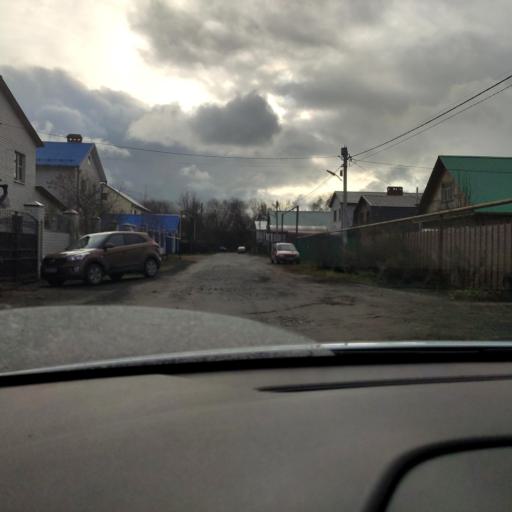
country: RU
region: Tatarstan
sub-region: Gorod Kazan'
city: Kazan
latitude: 55.8822
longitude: 49.0992
